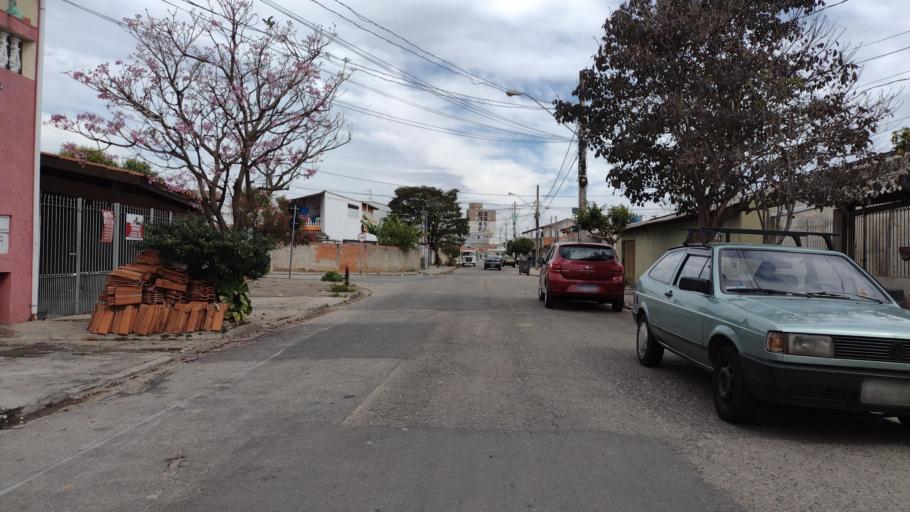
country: BR
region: Sao Paulo
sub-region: Sorocaba
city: Sorocaba
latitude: -23.4318
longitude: -47.4683
